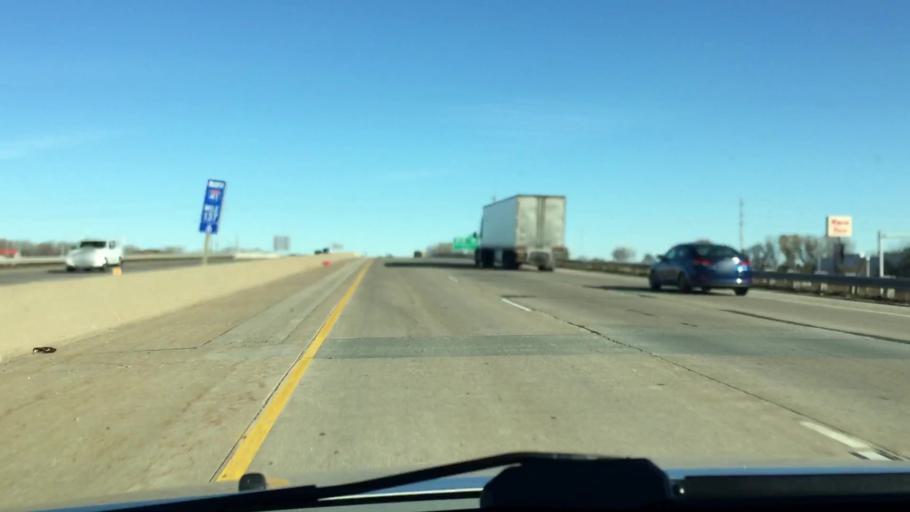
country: US
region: Wisconsin
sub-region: Outagamie County
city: Appleton
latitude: 44.2716
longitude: -88.4663
